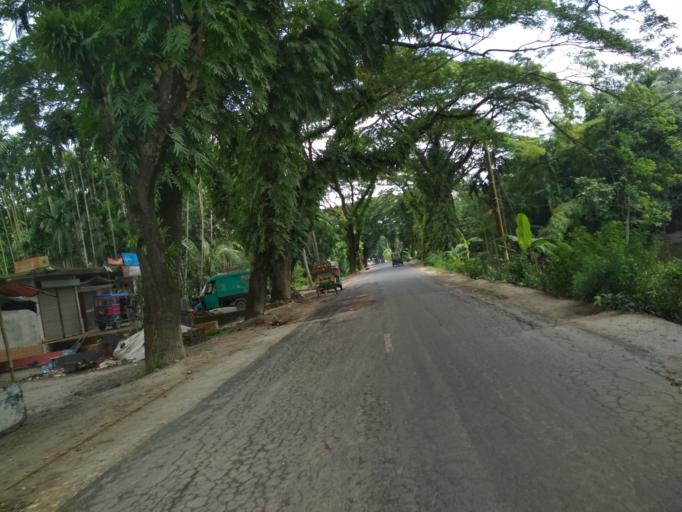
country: BD
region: Chittagong
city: Lakshmipur
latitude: 22.9619
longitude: 90.8096
